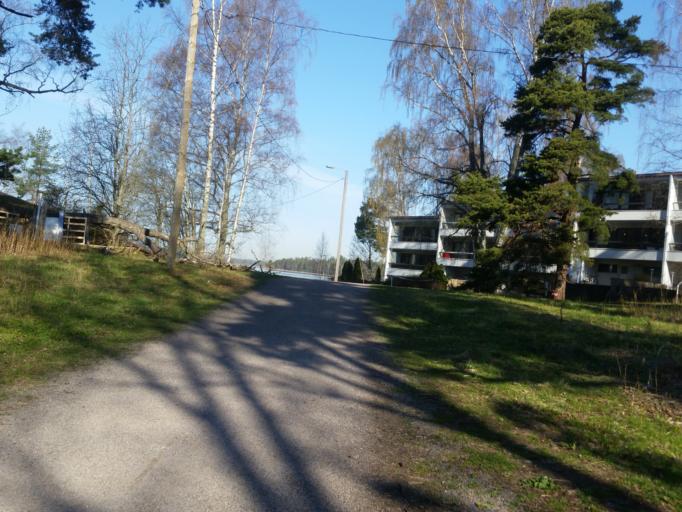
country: FI
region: Uusimaa
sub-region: Helsinki
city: Teekkarikylae
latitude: 60.1468
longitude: 24.8783
